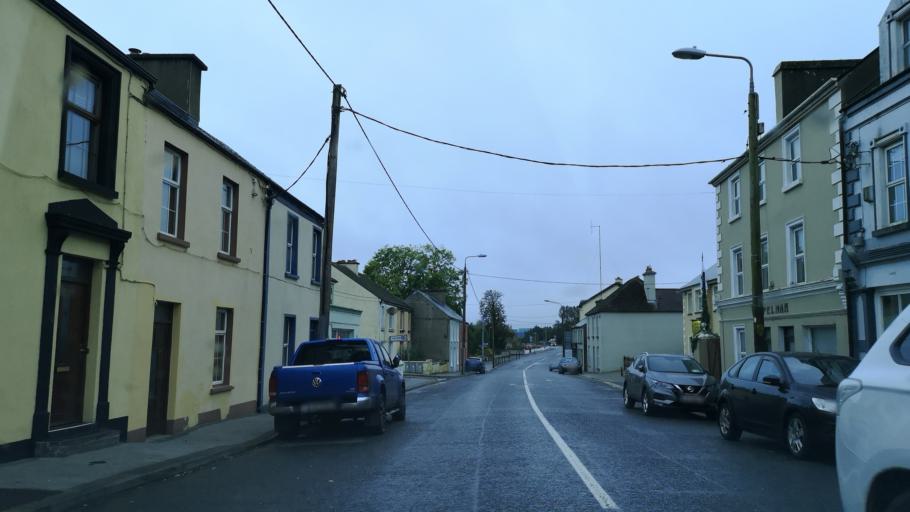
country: IE
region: Connaught
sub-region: Roscommon
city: Ballaghaderreen
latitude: 53.9013
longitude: -8.5771
